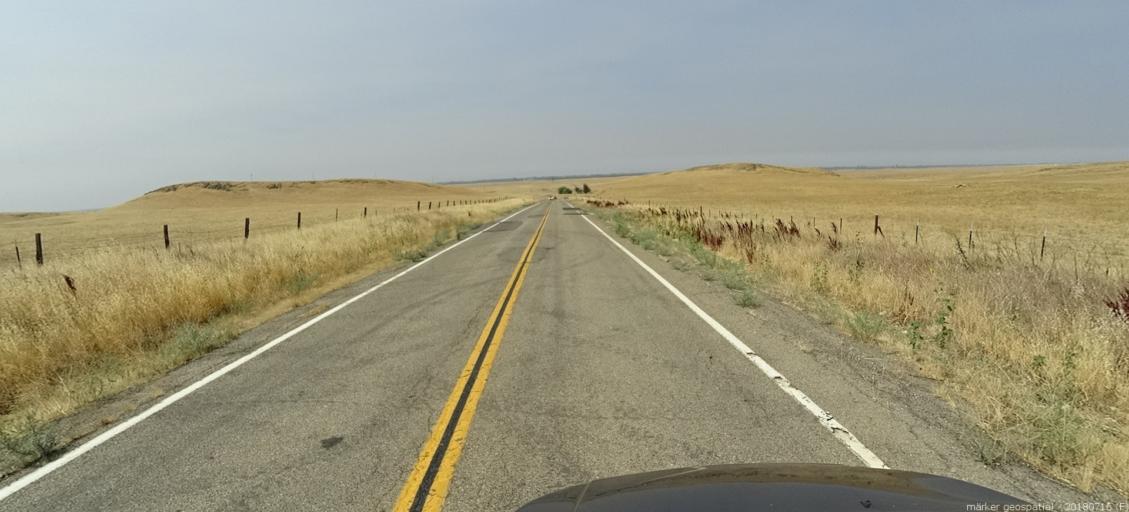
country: US
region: California
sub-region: Madera County
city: Bonadelle Ranchos-Madera Ranchos
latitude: 37.0927
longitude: -119.9516
